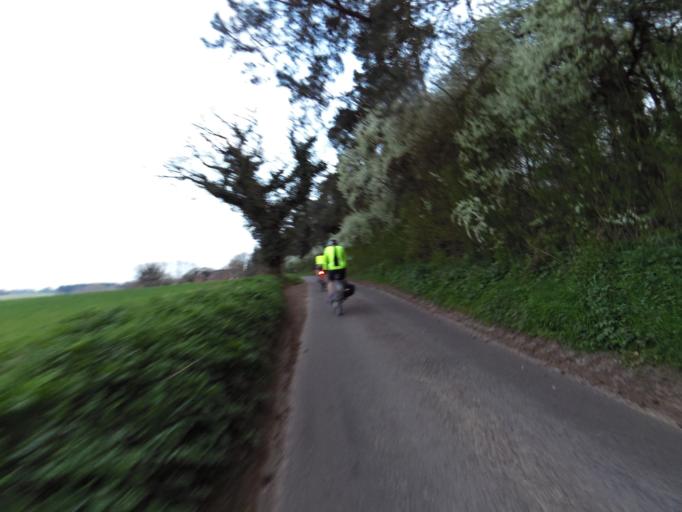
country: GB
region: England
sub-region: Suffolk
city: Kesgrave
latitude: 52.1037
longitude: 1.2492
